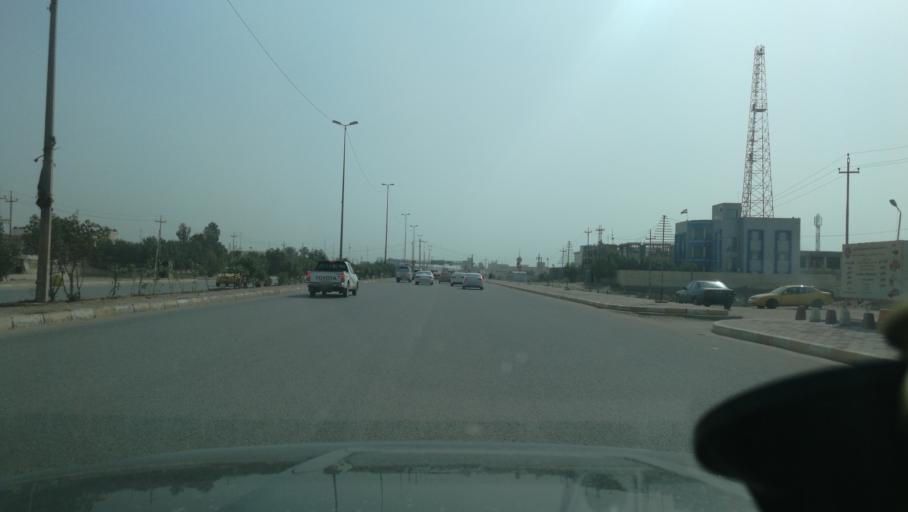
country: IQ
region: Dhi Qar
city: An Nasiriyah
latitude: 31.0625
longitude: 46.2483
